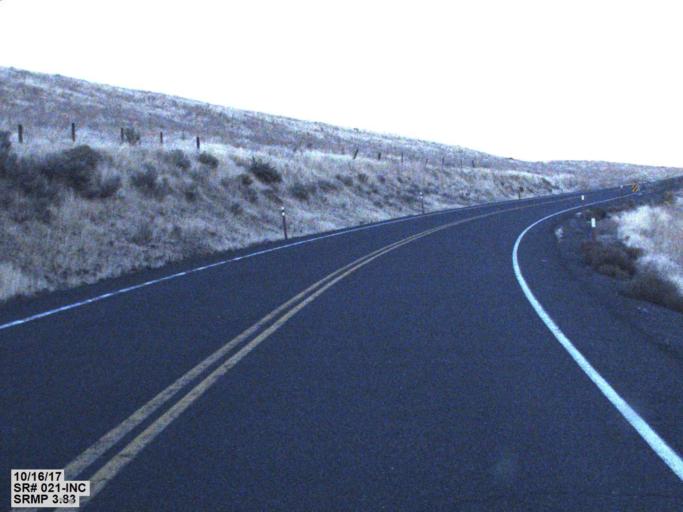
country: US
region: Washington
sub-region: Franklin County
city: Connell
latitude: 46.6926
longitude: -118.5294
